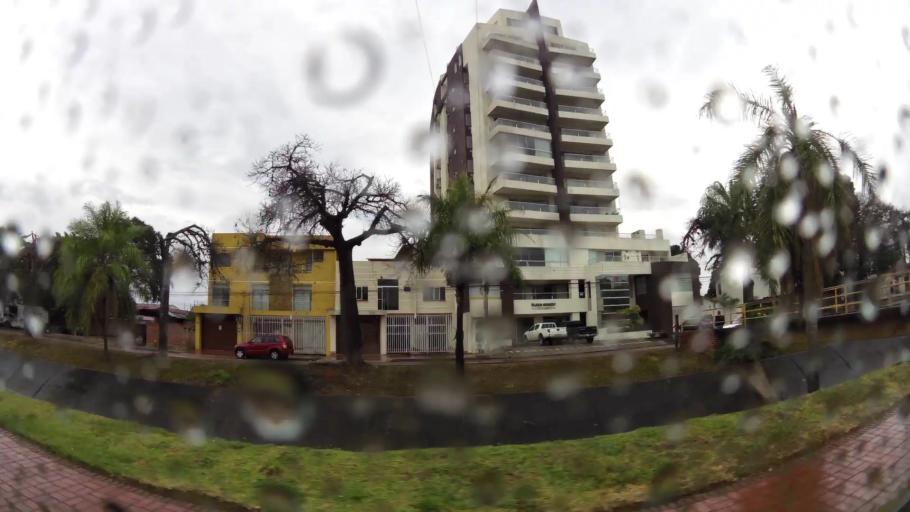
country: BO
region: Santa Cruz
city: Santa Cruz de la Sierra
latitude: -17.7777
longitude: -63.1623
